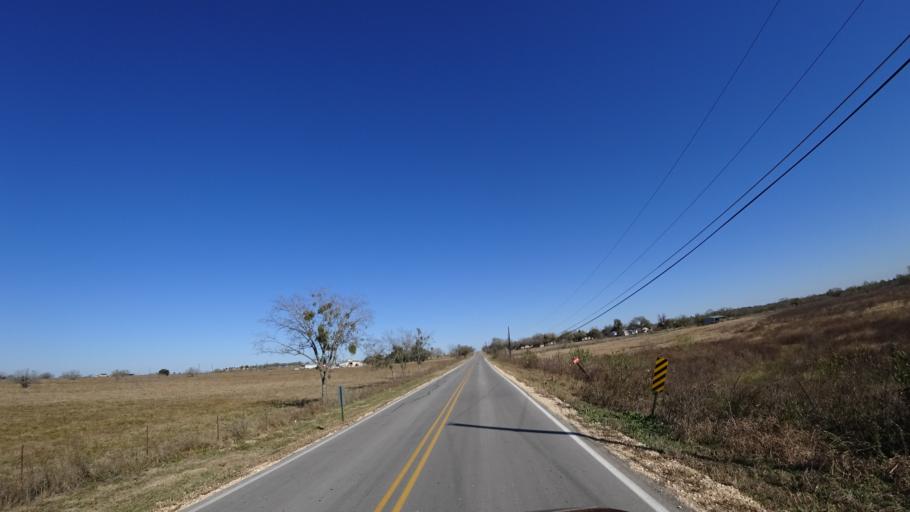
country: US
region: Texas
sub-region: Travis County
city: Garfield
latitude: 30.1142
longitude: -97.6491
